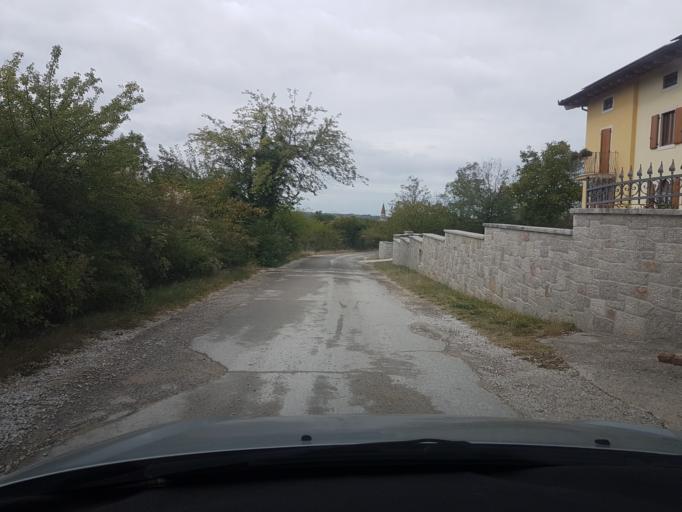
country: IT
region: Friuli Venezia Giulia
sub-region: Provincia di Gorizia
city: Doberdo del Lago
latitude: 45.8442
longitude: 13.5452
